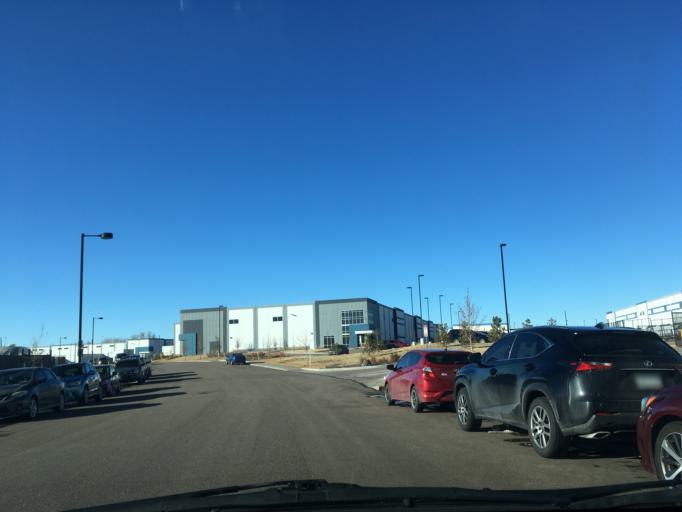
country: US
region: Colorado
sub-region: Adams County
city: Twin Lakes
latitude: 39.7934
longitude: -104.9822
